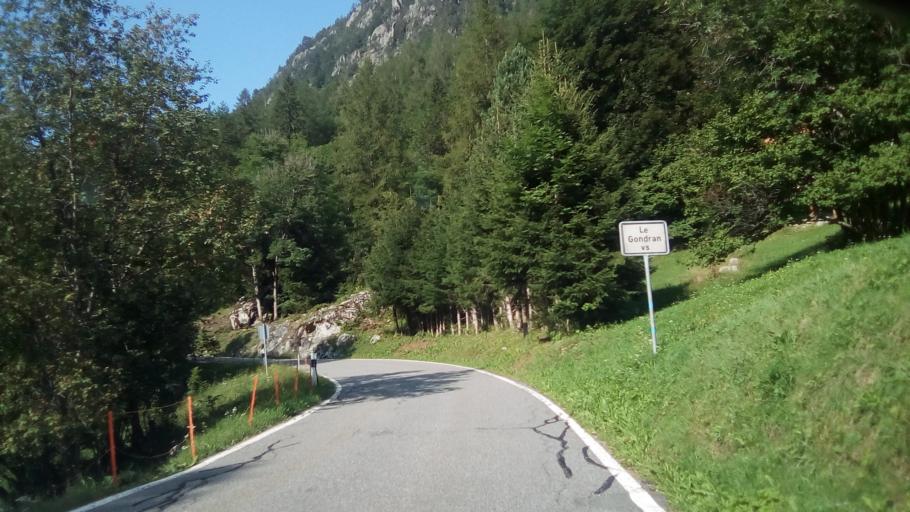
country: CH
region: Valais
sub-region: Martigny District
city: Martigny-Combe
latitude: 46.0539
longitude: 7.0822
